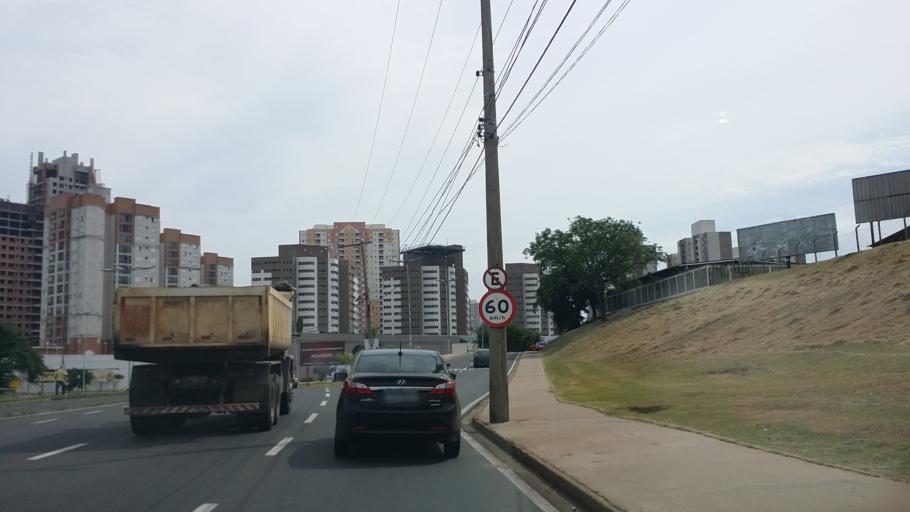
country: BR
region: Sao Paulo
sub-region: Indaiatuba
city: Indaiatuba
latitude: -23.0985
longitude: -47.2251
